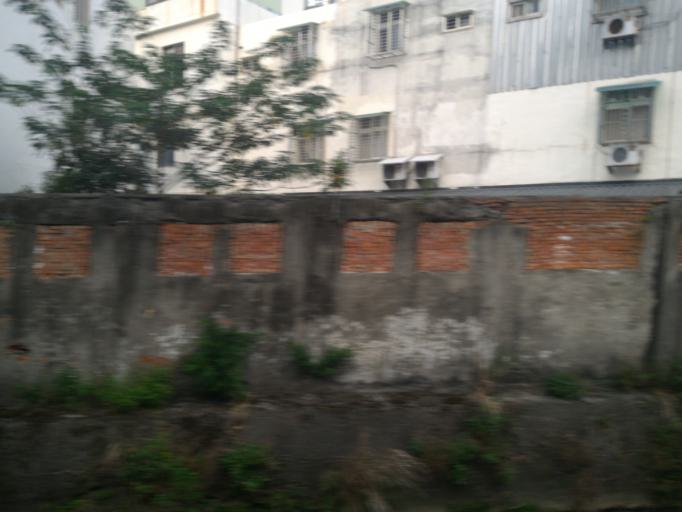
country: TW
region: Taiwan
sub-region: Taoyuan
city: Taoyuan
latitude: 24.9787
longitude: 121.3304
